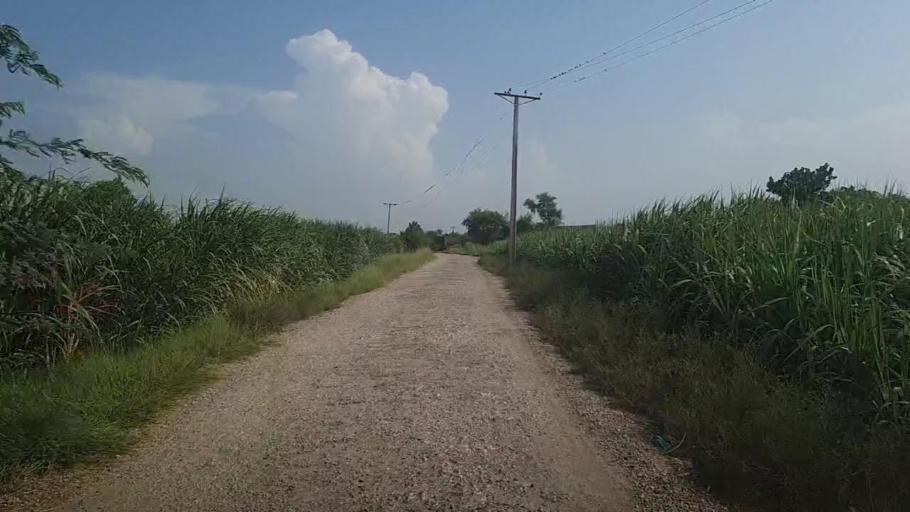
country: PK
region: Sindh
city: Ubauro
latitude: 28.1691
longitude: 69.7738
